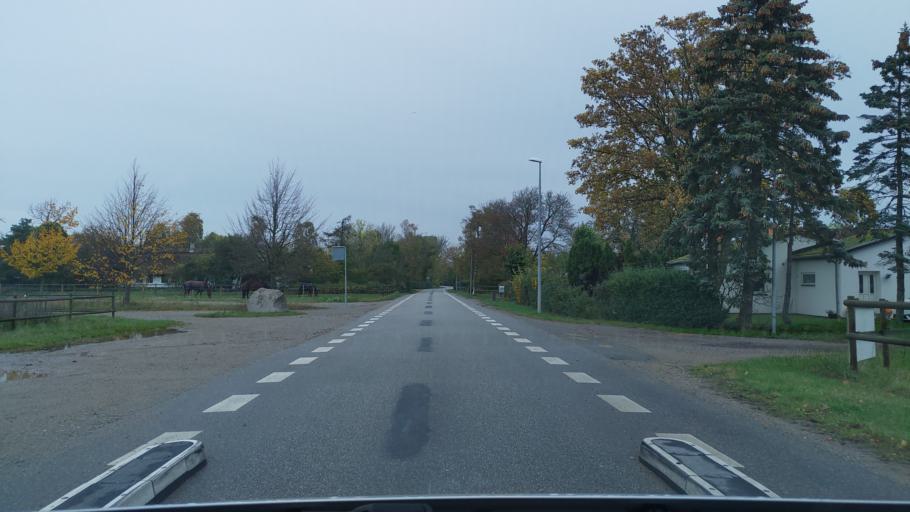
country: DK
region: Capital Region
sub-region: Tarnby Kommune
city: Tarnby
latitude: 55.5804
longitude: 12.6006
